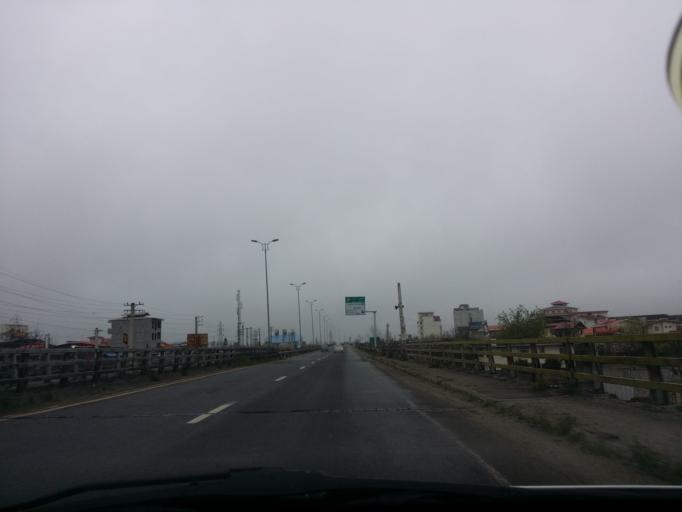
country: IR
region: Mazandaran
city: Tonekabon
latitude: 36.8084
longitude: 50.8656
